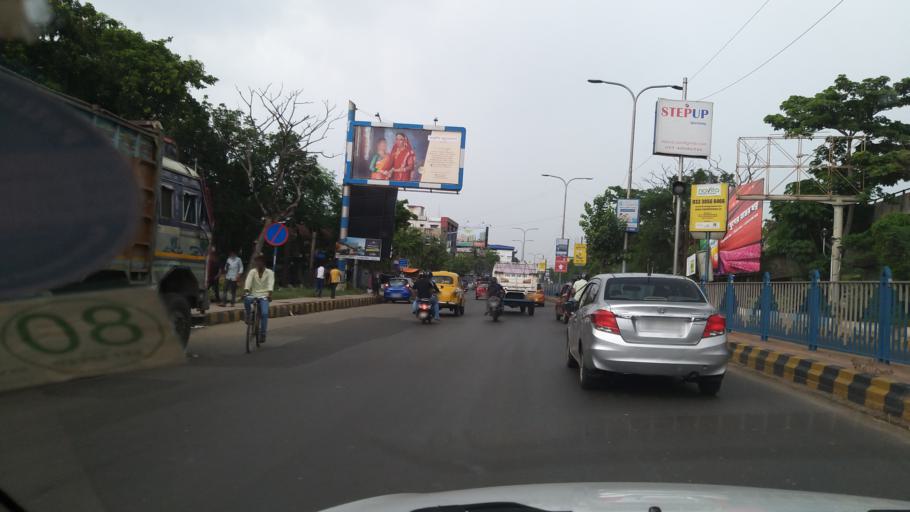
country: IN
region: West Bengal
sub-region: North 24 Parganas
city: Dam Dam
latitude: 22.6540
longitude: 88.4391
